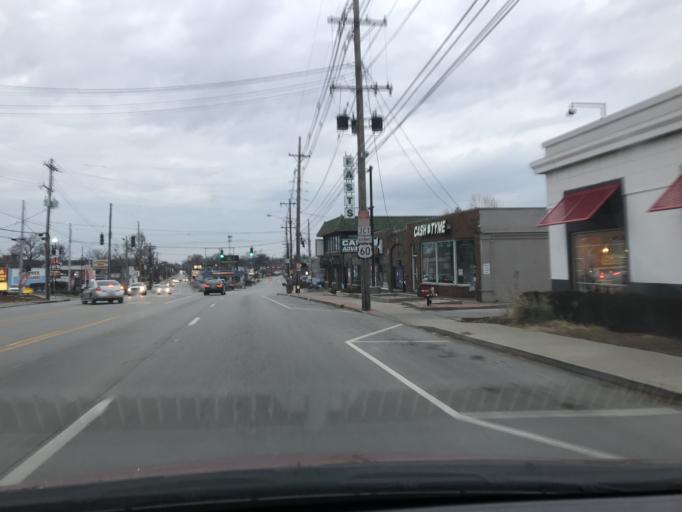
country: US
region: Kentucky
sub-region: Jefferson County
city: Audubon Park
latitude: 38.2125
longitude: -85.7411
